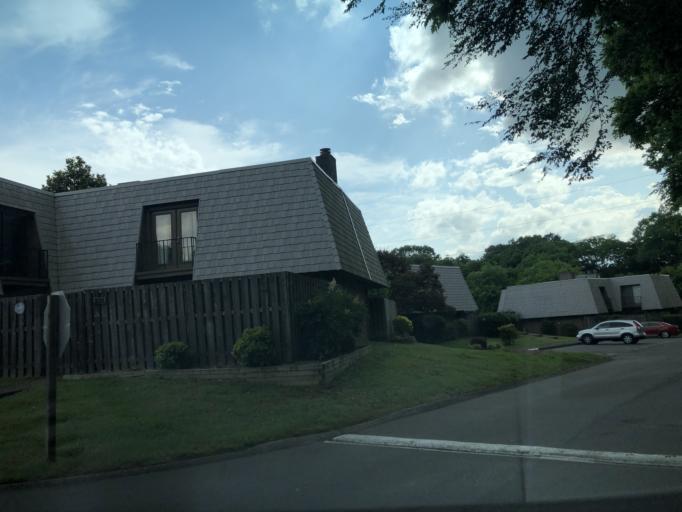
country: US
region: Tennessee
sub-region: Davidson County
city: Goodlettsville
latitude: 36.2762
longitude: -86.7012
